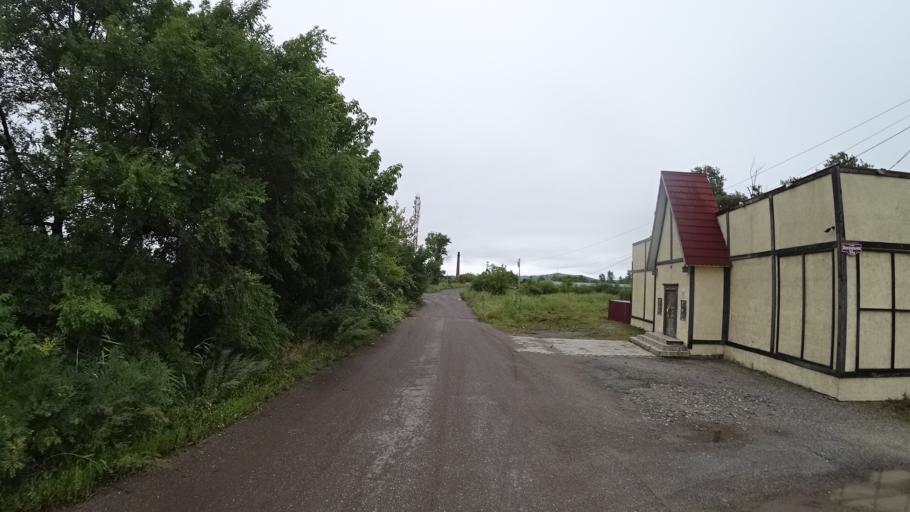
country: RU
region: Primorskiy
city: Monastyrishche
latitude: 44.2063
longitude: 132.4414
